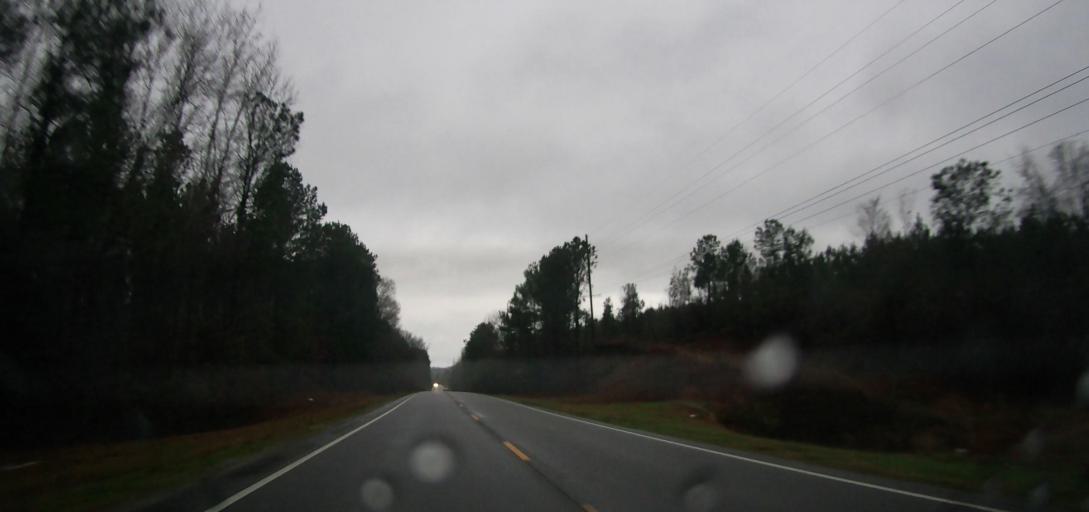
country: US
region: Alabama
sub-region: Bibb County
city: West Blocton
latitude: 33.0996
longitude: -87.1381
